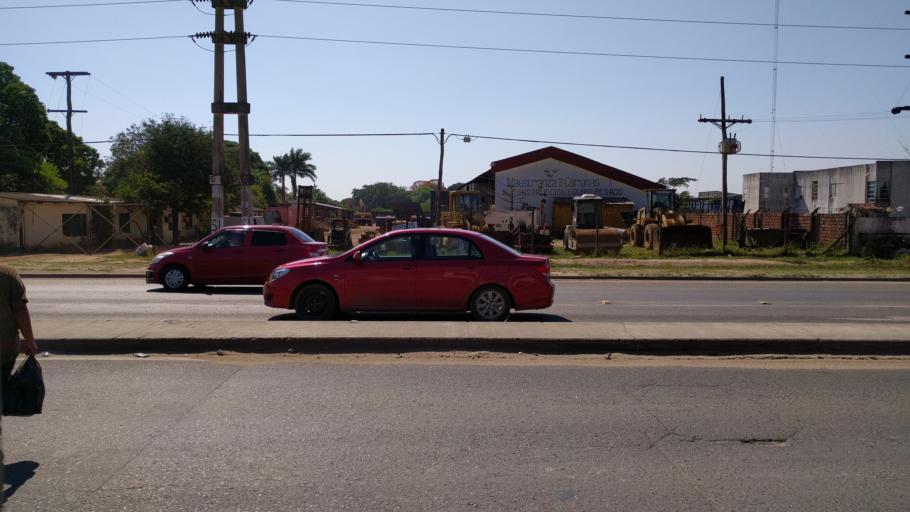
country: BO
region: Santa Cruz
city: Santa Cruz de la Sierra
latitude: -17.7660
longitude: -63.1074
